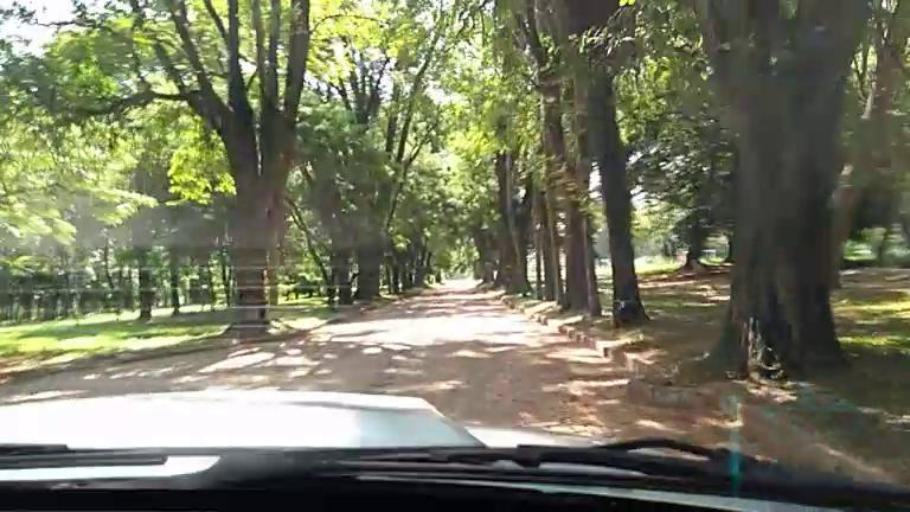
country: PY
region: Asuncion
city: Asuncion
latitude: -25.2476
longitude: -57.5751
